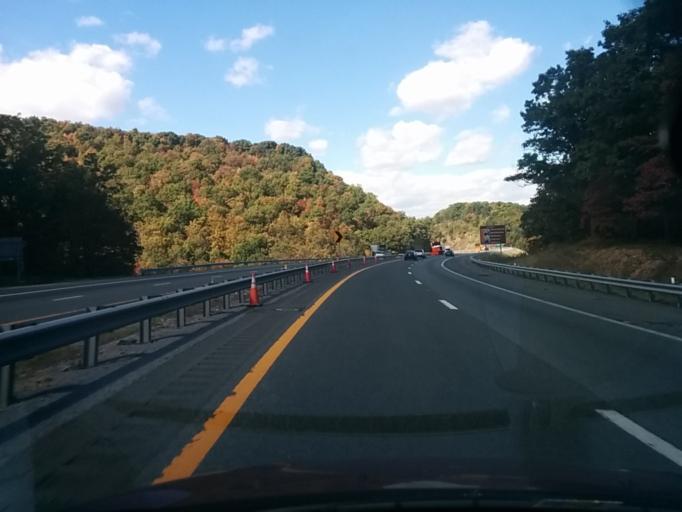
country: US
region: Virginia
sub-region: City of Waynesboro
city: Waynesboro
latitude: 38.0349
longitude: -78.8695
